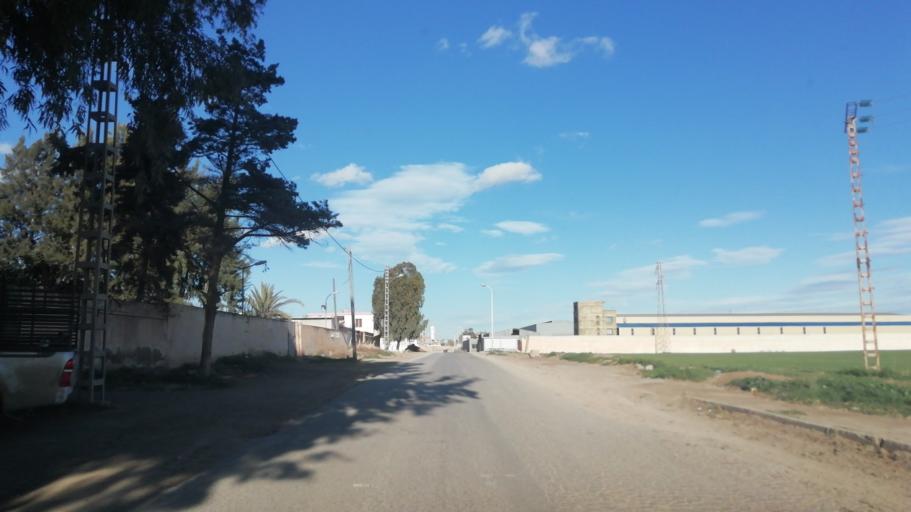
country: DZ
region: Oran
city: Sidi ech Chahmi
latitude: 35.6377
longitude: -0.5484
